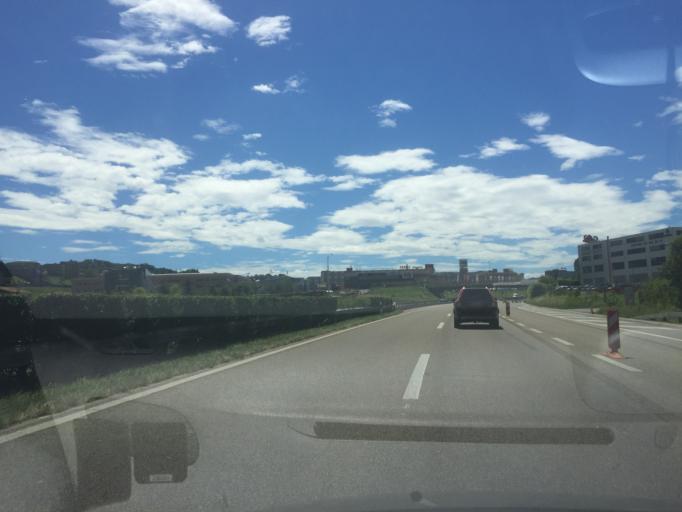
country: CH
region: Ticino
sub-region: Mendrisio District
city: Mendrisio
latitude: 45.8800
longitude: 8.9807
